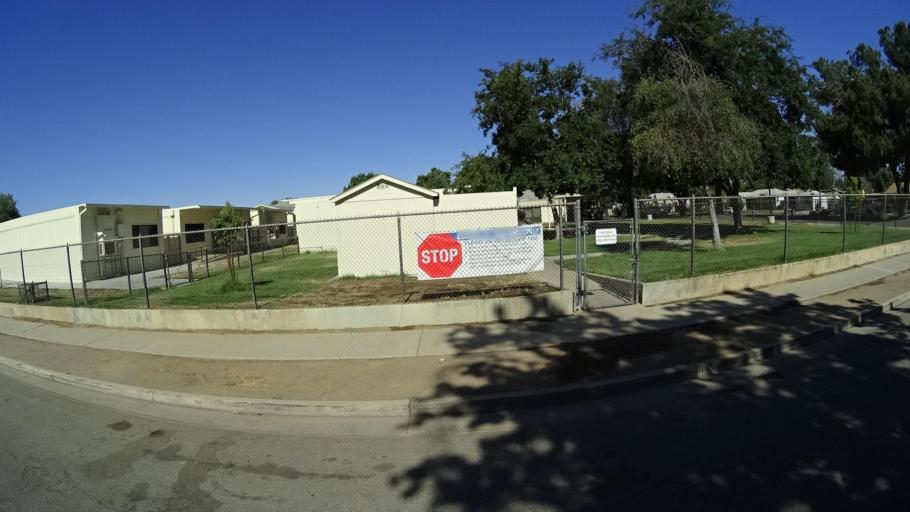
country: US
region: California
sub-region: Fresno County
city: Fresno
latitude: 36.7155
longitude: -119.7863
